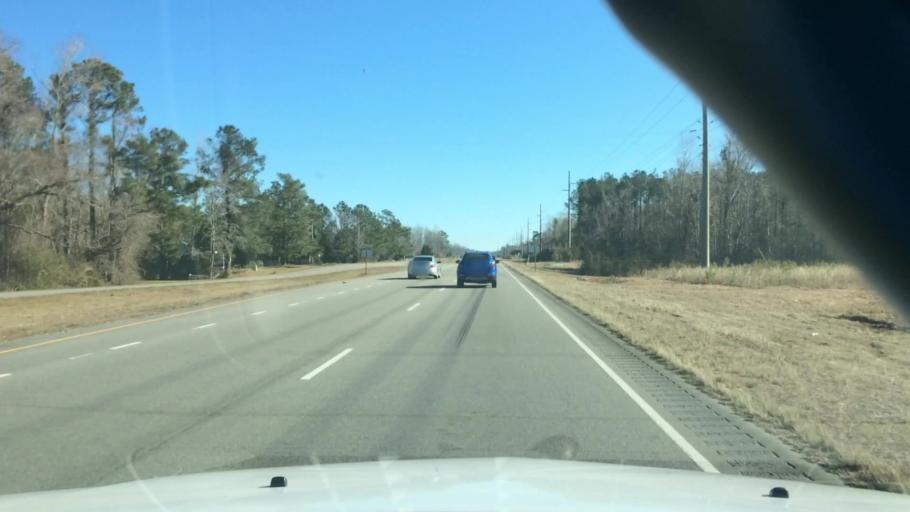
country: US
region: North Carolina
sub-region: Brunswick County
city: Shallotte
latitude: 34.0039
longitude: -78.3106
